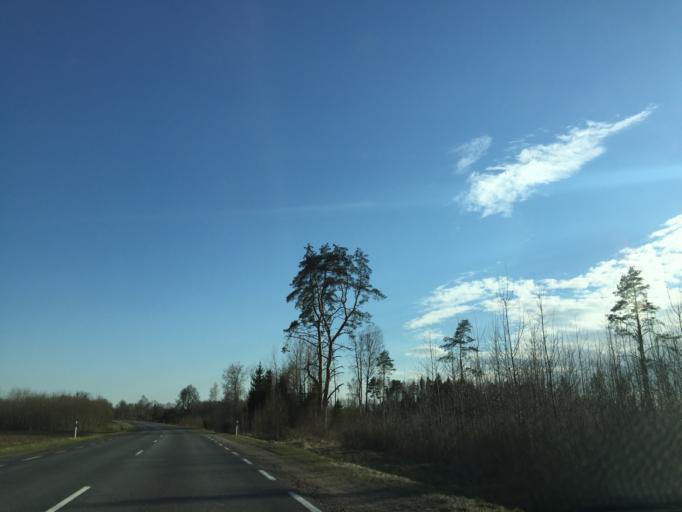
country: EE
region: Valgamaa
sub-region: Torva linn
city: Torva
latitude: 58.1653
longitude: 25.9625
